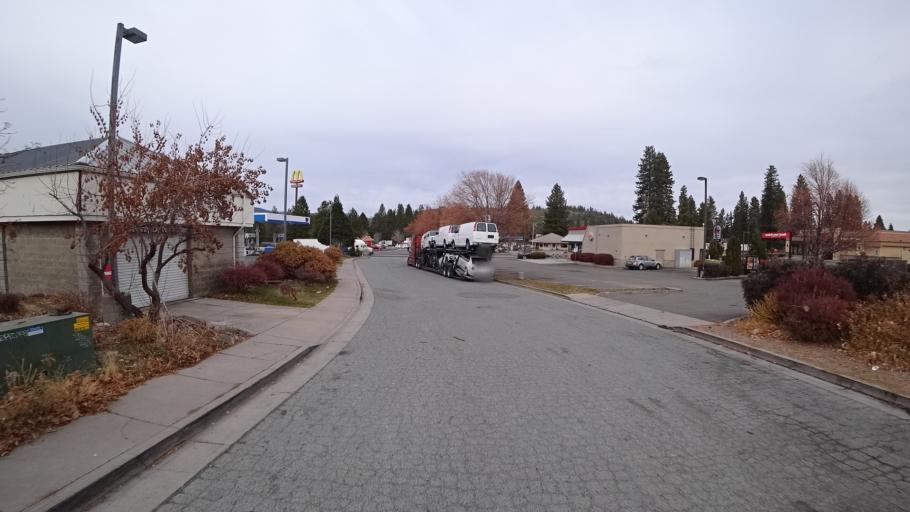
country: US
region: California
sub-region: Siskiyou County
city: Weed
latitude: 41.3970
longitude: -122.3777
